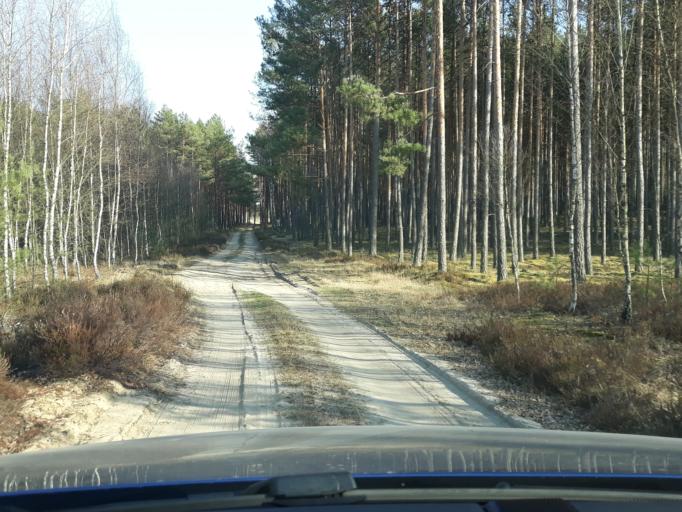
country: PL
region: Pomeranian Voivodeship
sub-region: Powiat bytowski
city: Lipnica
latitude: 53.9158
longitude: 17.4743
